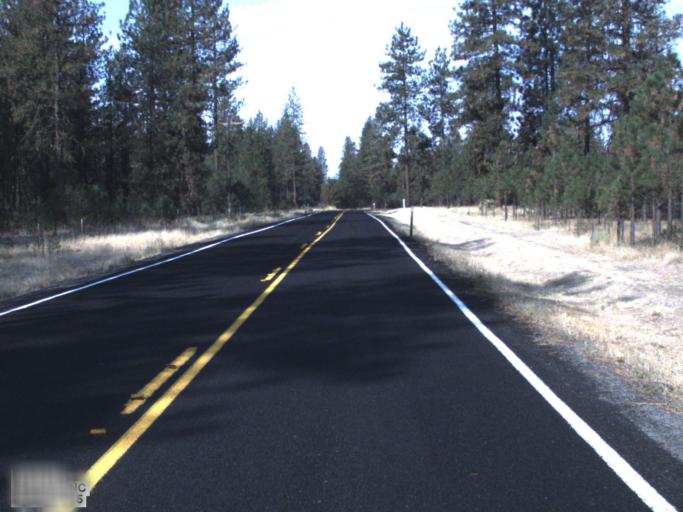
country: US
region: Washington
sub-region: Spokane County
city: Fairchild Air Force Base
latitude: 47.8395
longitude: -117.8309
